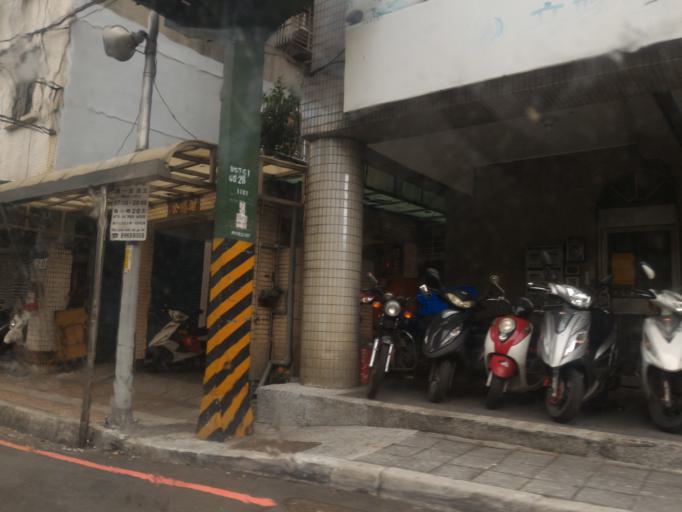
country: TW
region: Taipei
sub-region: Taipei
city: Banqiao
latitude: 25.0885
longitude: 121.4666
